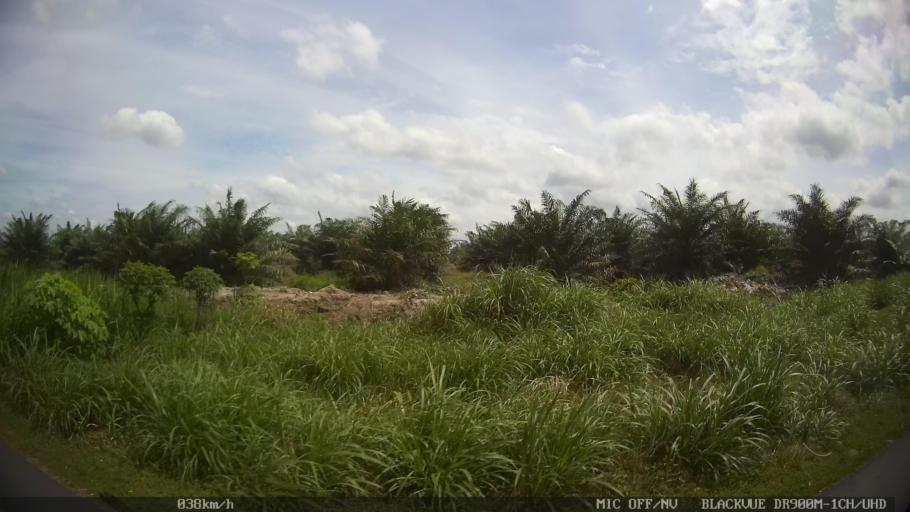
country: ID
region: North Sumatra
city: Percut
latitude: 3.5892
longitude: 98.8701
